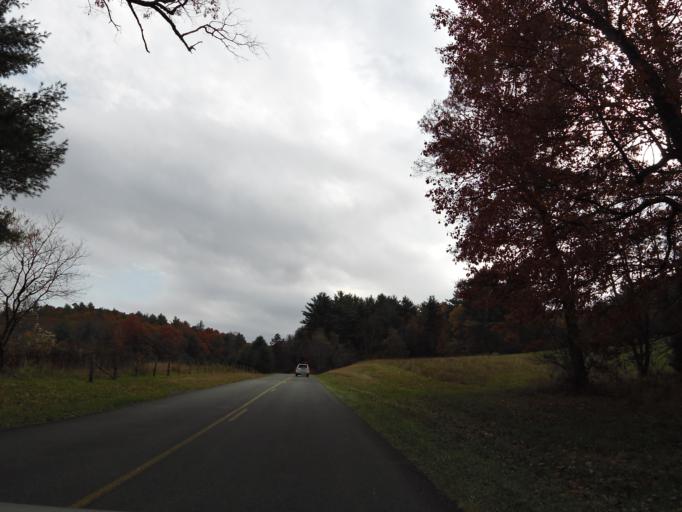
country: US
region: Virginia
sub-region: City of Galax
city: Galax
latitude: 36.5797
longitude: -80.8576
